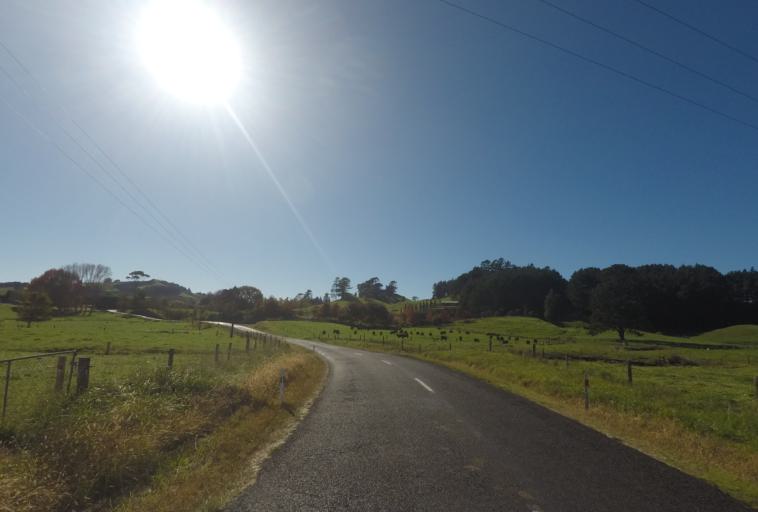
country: NZ
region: Bay of Plenty
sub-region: Western Bay of Plenty District
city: Waihi Beach
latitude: -37.4056
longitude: 175.9041
